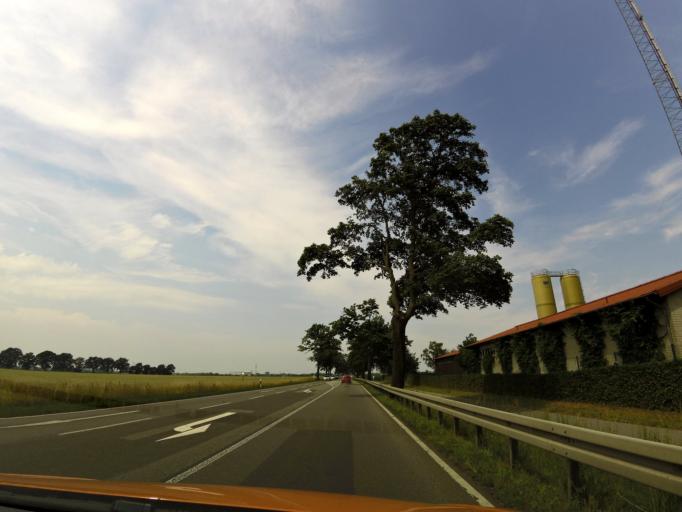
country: DE
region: Brandenburg
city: Kyritz
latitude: 52.9253
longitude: 12.4223
